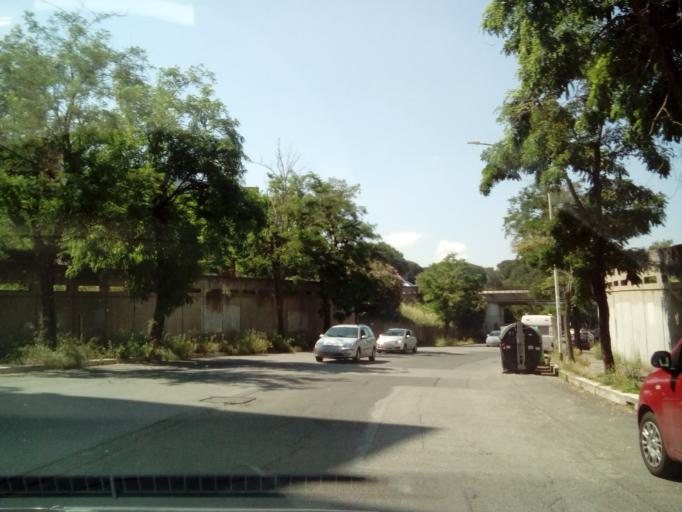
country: IT
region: Latium
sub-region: Citta metropolitana di Roma Capitale
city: Rome
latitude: 41.8895
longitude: 12.5872
